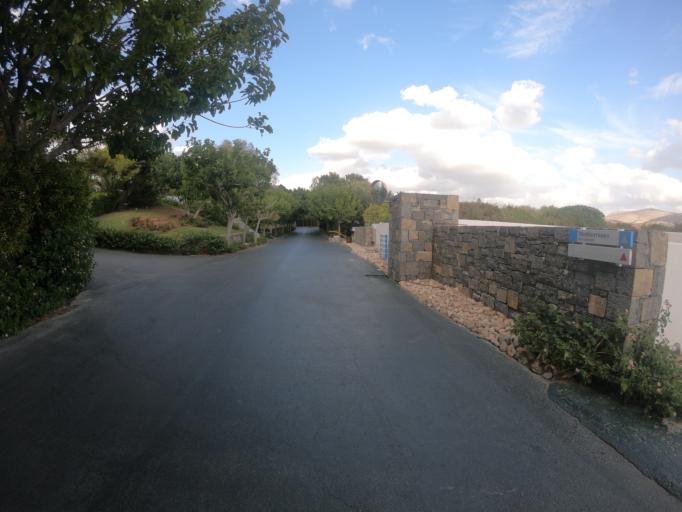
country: GR
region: Attica
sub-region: Nomarchia Anatolikis Attikis
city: Saronida
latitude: 37.7775
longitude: 23.8884
